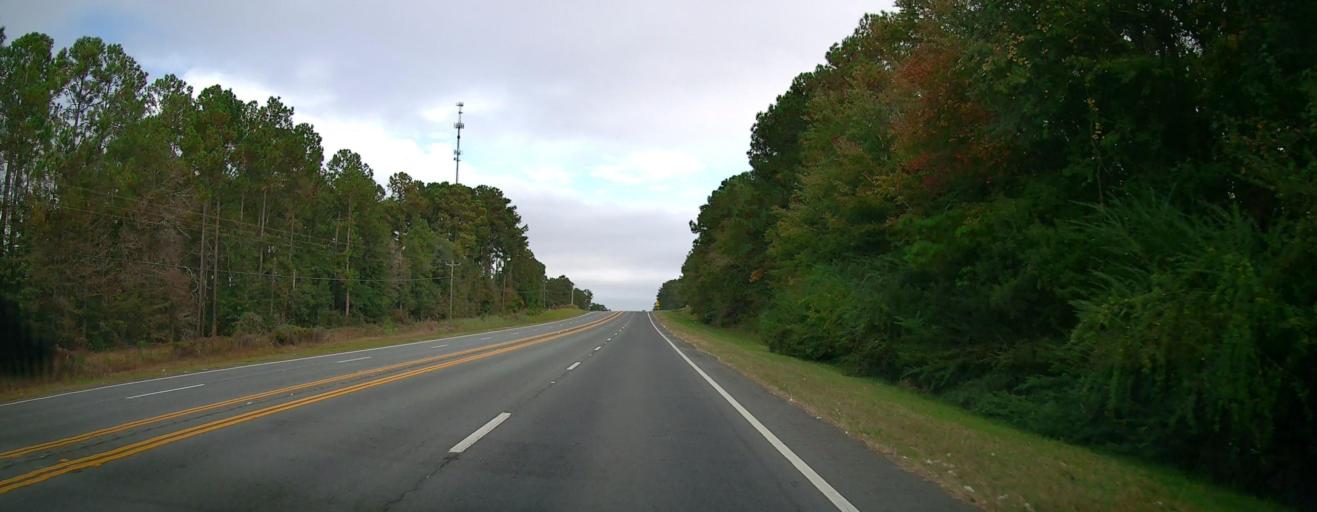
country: US
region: Georgia
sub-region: Tift County
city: Omega
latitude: 31.3850
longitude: -83.5507
